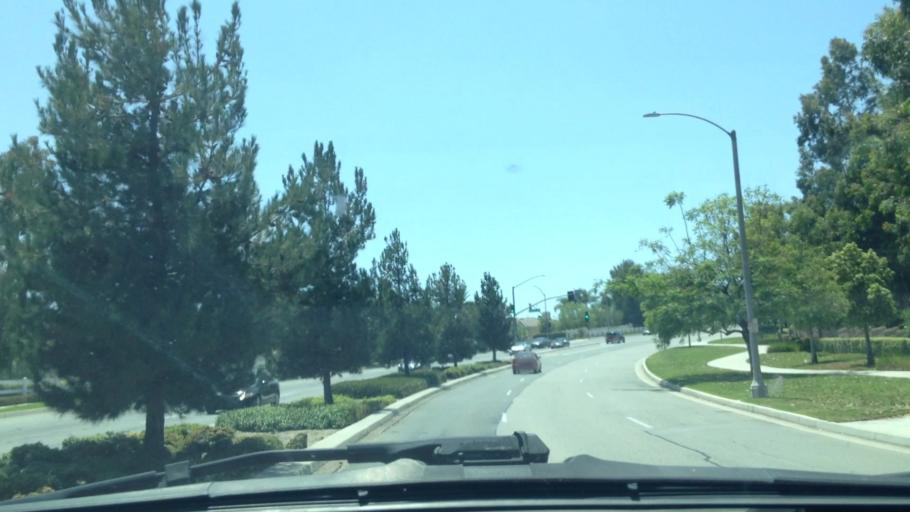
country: US
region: California
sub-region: Orange County
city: Brea
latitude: 33.9017
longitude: -117.8899
